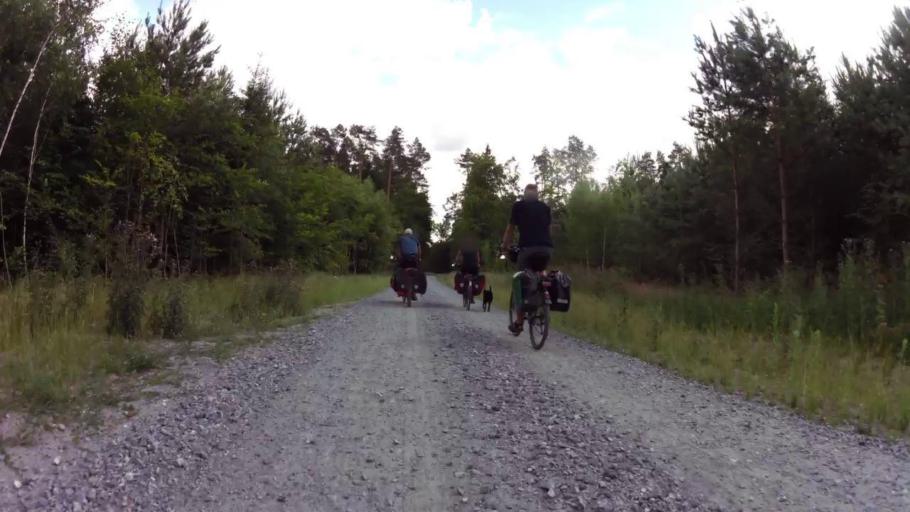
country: PL
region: West Pomeranian Voivodeship
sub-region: Powiat lobeski
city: Lobez
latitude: 53.6851
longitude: 15.5482
